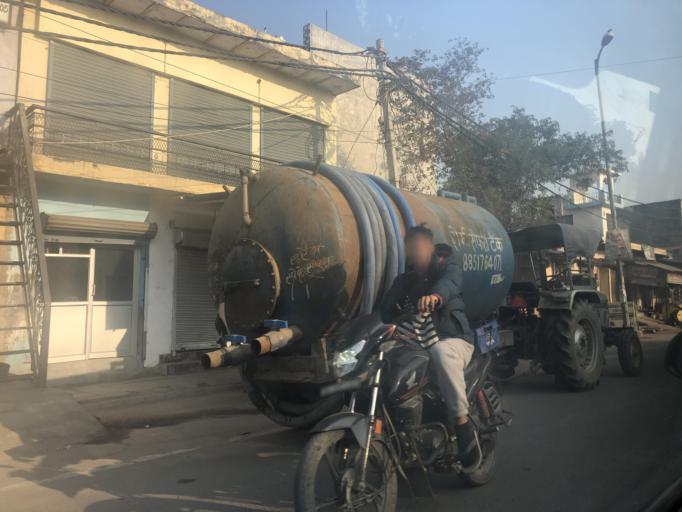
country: IN
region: Haryana
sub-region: Gurgaon
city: Gurgaon
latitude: 28.5574
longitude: 77.0047
